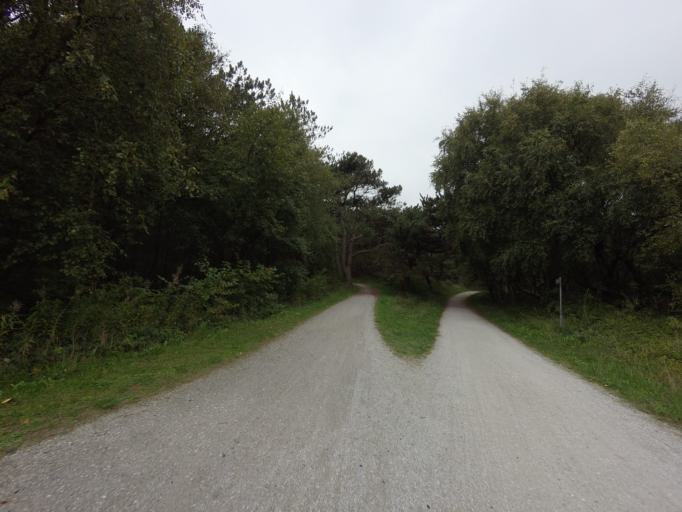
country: NL
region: Friesland
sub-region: Gemeente Schiermonnikoog
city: Schiermonnikoog
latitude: 53.4951
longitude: 6.1704
